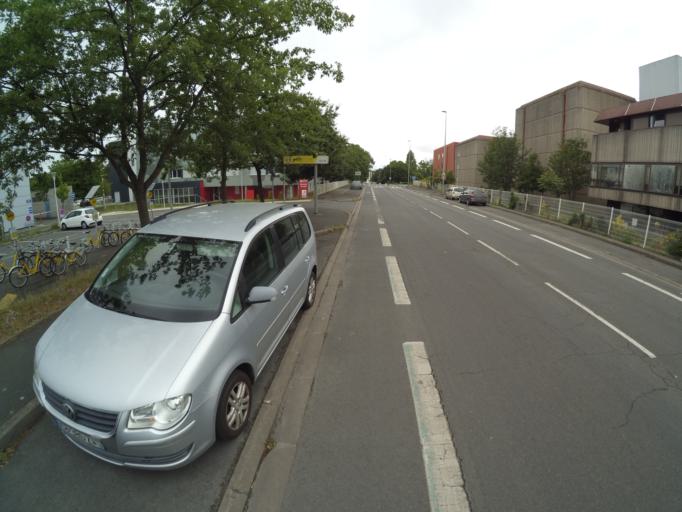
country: FR
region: Poitou-Charentes
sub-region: Departement de la Charente-Maritime
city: La Rochelle
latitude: 46.1402
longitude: -1.1537
